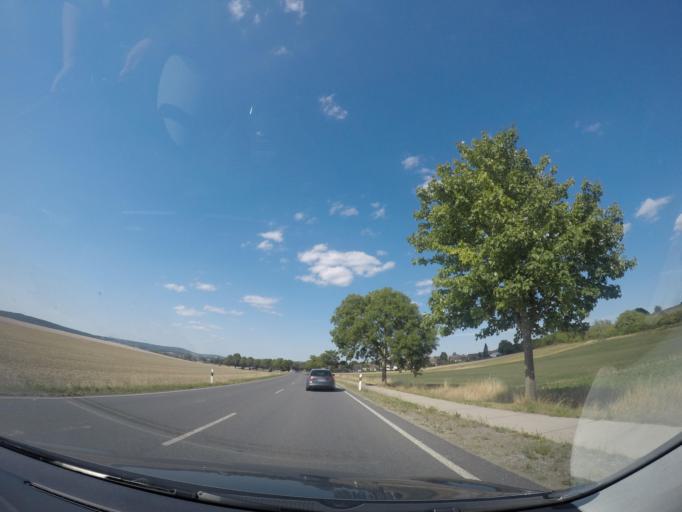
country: DE
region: Lower Saxony
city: Seesen
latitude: 51.8598
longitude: 10.1806
